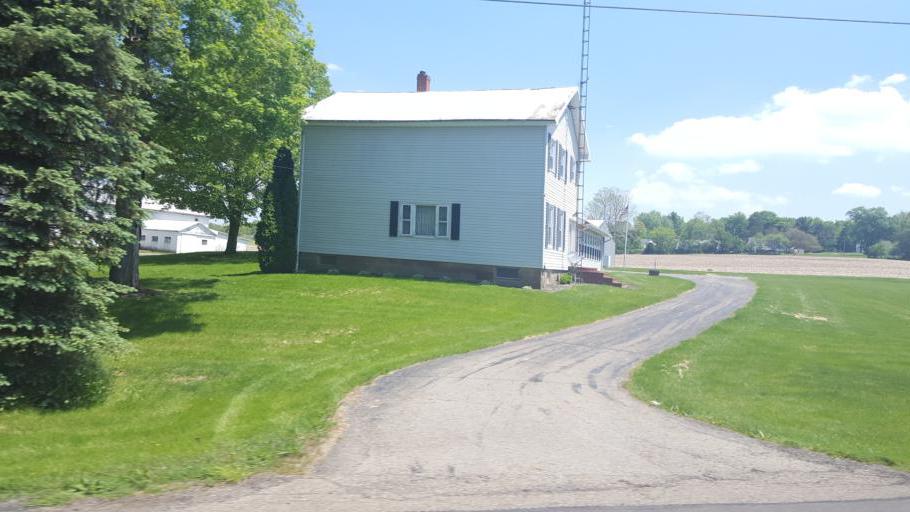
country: US
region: Ohio
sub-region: Knox County
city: Mount Vernon
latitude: 40.4131
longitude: -82.4993
